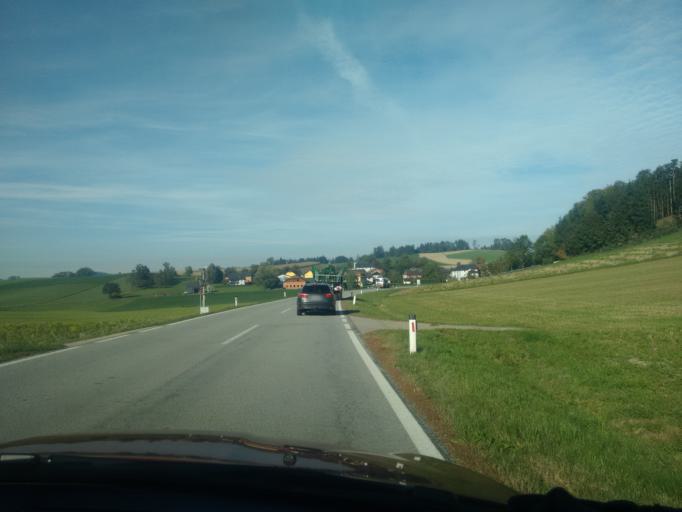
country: AT
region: Upper Austria
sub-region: Politischer Bezirk Vocklabruck
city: Rutzenham
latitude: 48.0610
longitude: 13.7233
